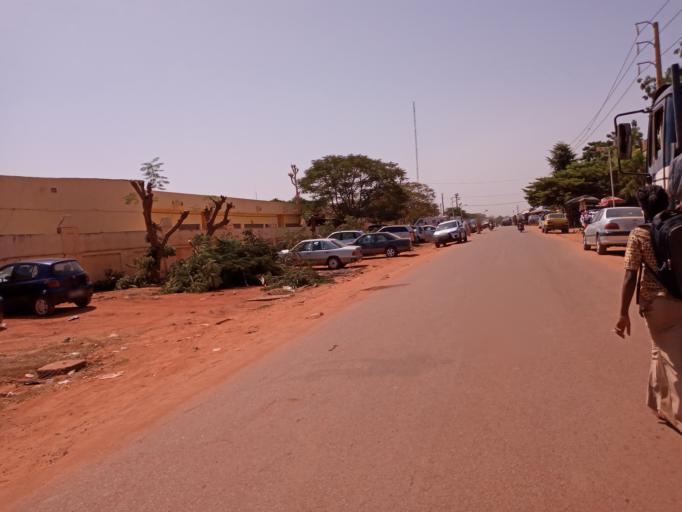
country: ML
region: Bamako
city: Bamako
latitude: 12.6126
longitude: -7.9948
